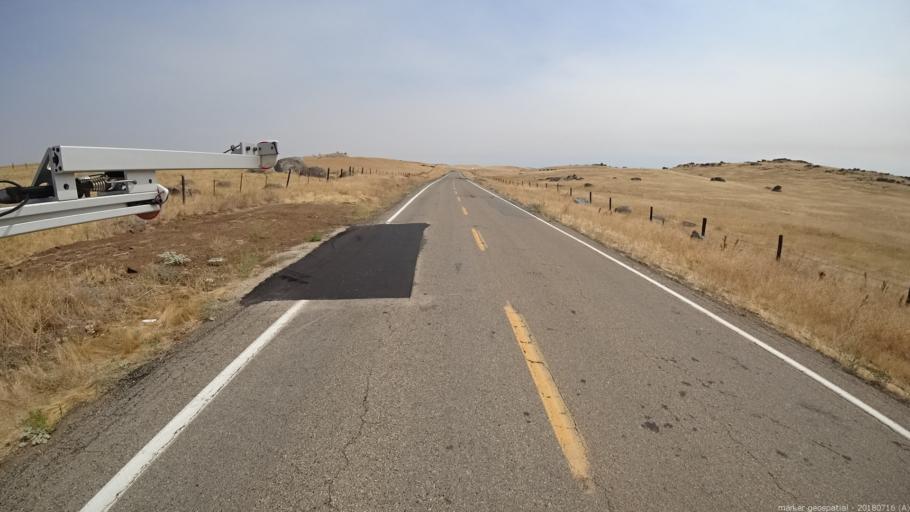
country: US
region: California
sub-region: Madera County
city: Bonadelle Ranchos-Madera Ranchos
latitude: 37.1111
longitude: -119.9392
